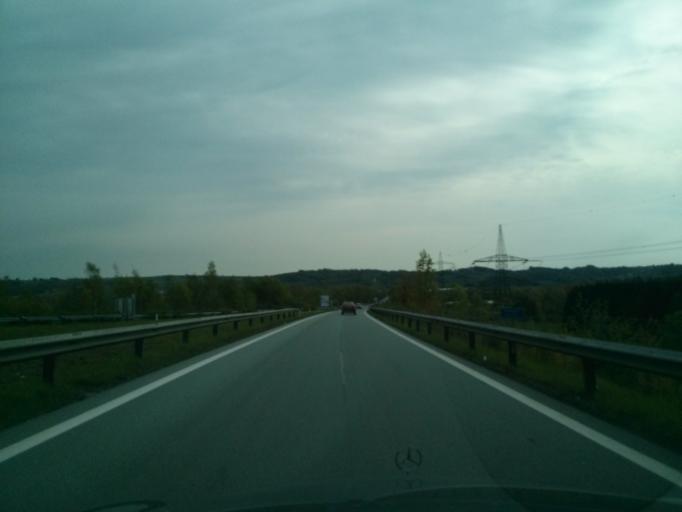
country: AT
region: Burgenland
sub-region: Politischer Bezirk Oberwart
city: Markt Allhau
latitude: 47.2804
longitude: 16.0646
